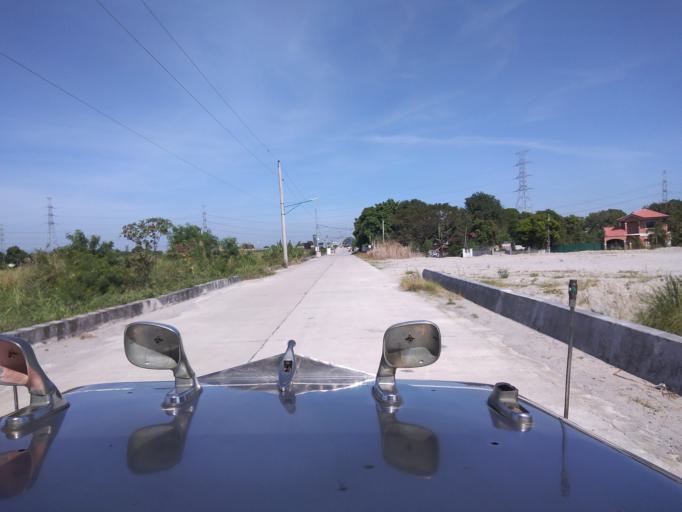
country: PH
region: Central Luzon
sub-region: Province of Pampanga
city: Bacolor
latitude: 15.0050
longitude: 120.6597
